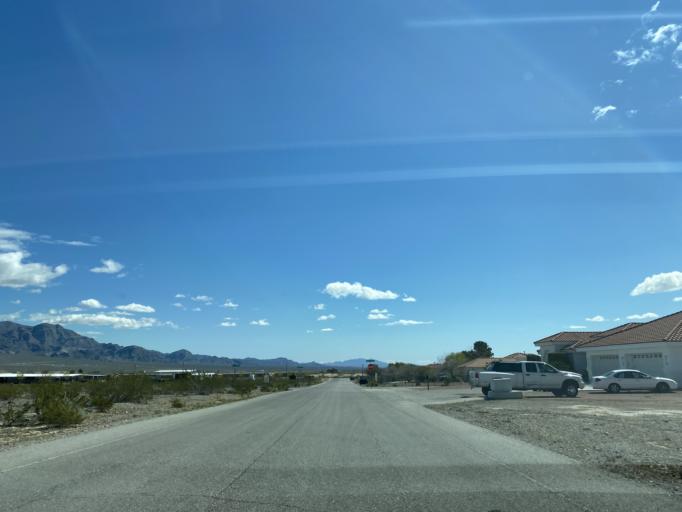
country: US
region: Nevada
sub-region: Clark County
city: North Las Vegas
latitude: 36.3266
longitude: -115.2817
